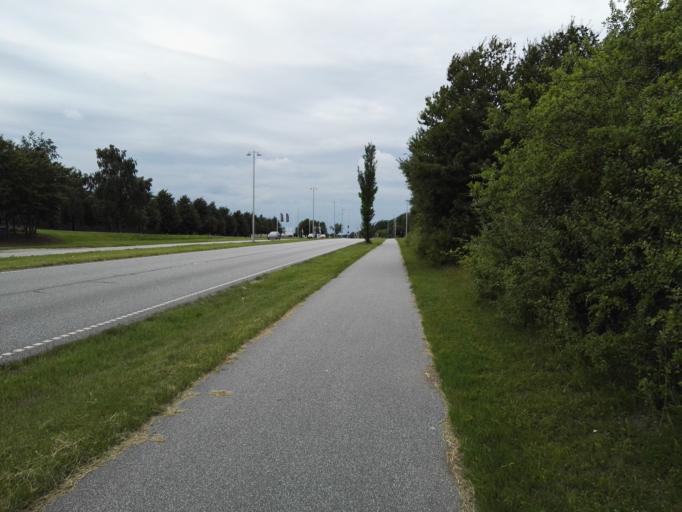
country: DK
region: Capital Region
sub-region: Egedal Kommune
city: Smorumnedre
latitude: 55.7524
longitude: 12.3029
